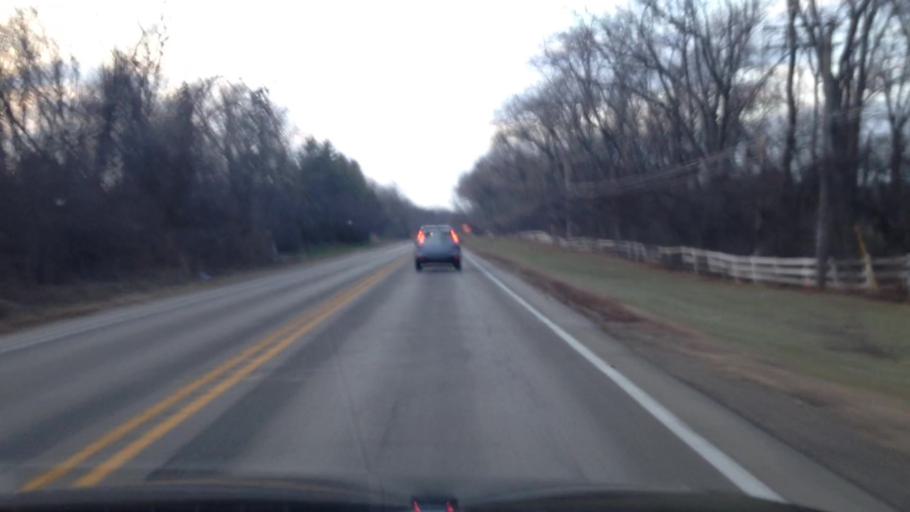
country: US
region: Illinois
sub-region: Kane County
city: Carpentersville
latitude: 42.1347
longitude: -88.2340
